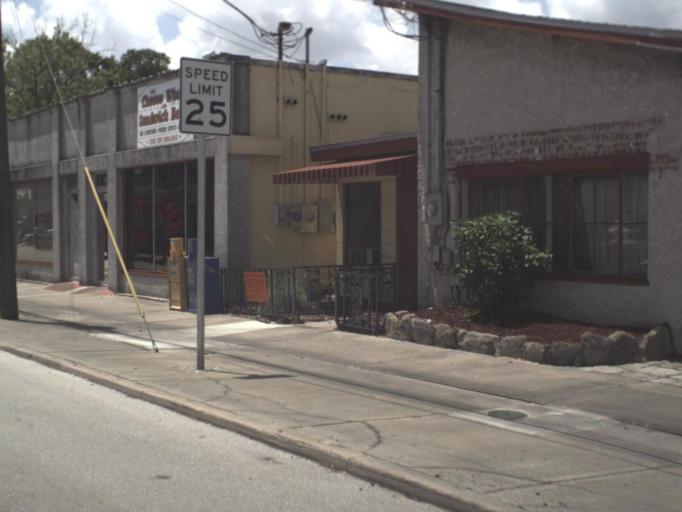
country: US
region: Florida
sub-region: Saint Johns County
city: Saint Augustine
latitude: 29.9169
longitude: -81.3227
